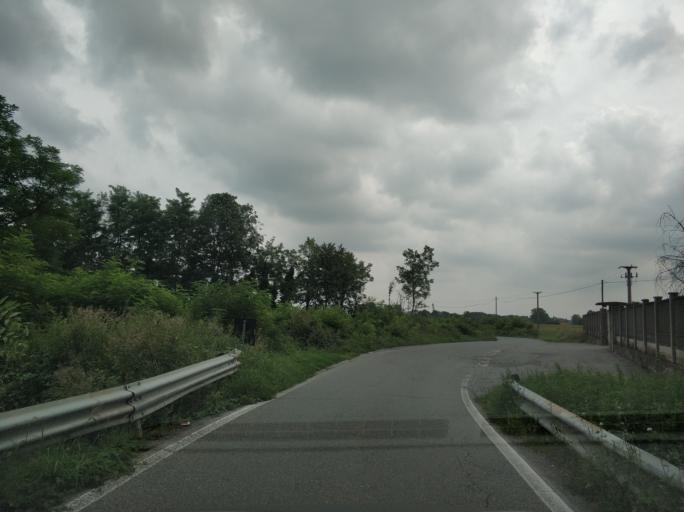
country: IT
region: Piedmont
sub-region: Provincia di Torino
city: Caselle Torinese
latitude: 45.1880
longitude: 7.6227
